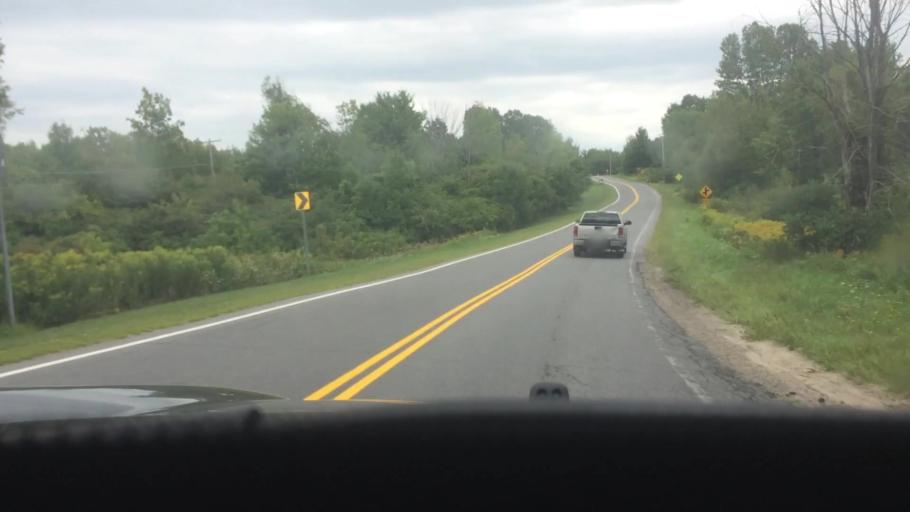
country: US
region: New York
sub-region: St. Lawrence County
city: Canton
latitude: 44.5350
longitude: -75.1751
